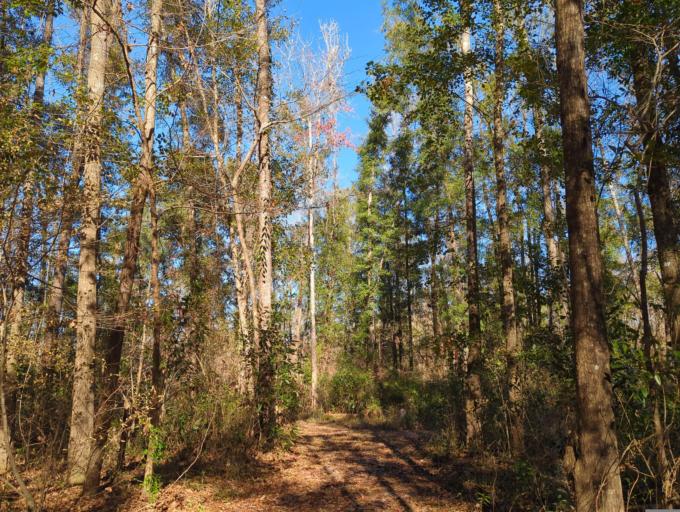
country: US
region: Florida
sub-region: Wakulla County
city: Crawfordville
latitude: 30.1844
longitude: -84.3258
